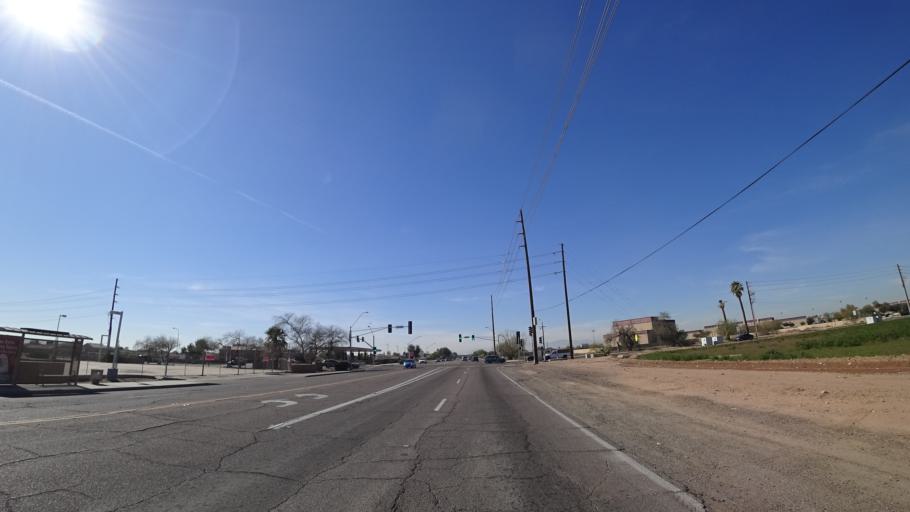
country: US
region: Arizona
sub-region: Maricopa County
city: Tolleson
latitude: 33.5089
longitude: -112.2540
